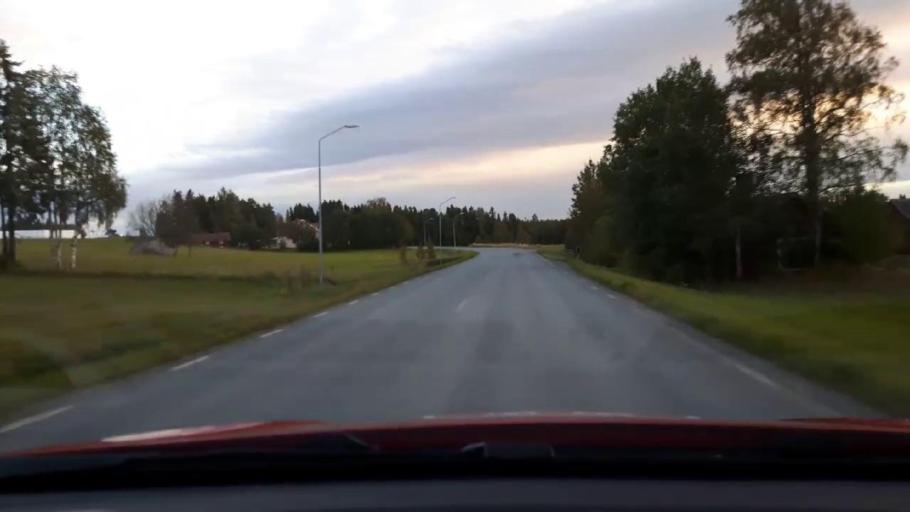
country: SE
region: Jaemtland
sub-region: OEstersunds Kommun
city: Ostersund
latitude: 63.0848
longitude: 14.4376
